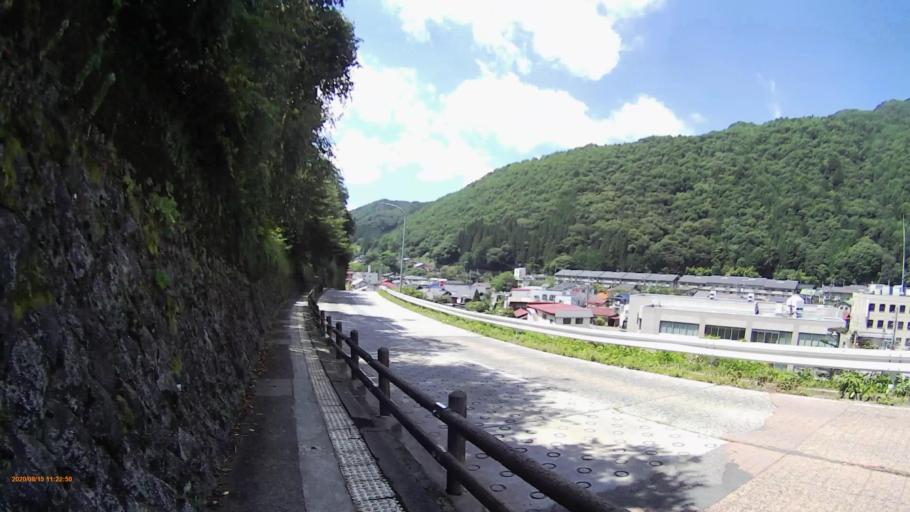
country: JP
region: Nagano
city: Ina
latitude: 35.8433
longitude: 137.6921
